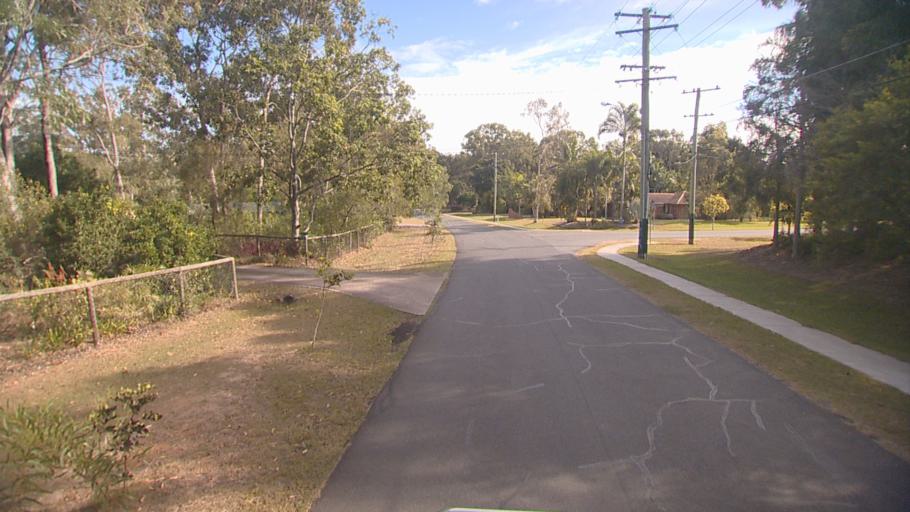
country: AU
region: Queensland
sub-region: Brisbane
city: Forest Lake
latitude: -27.6641
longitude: 153.0026
